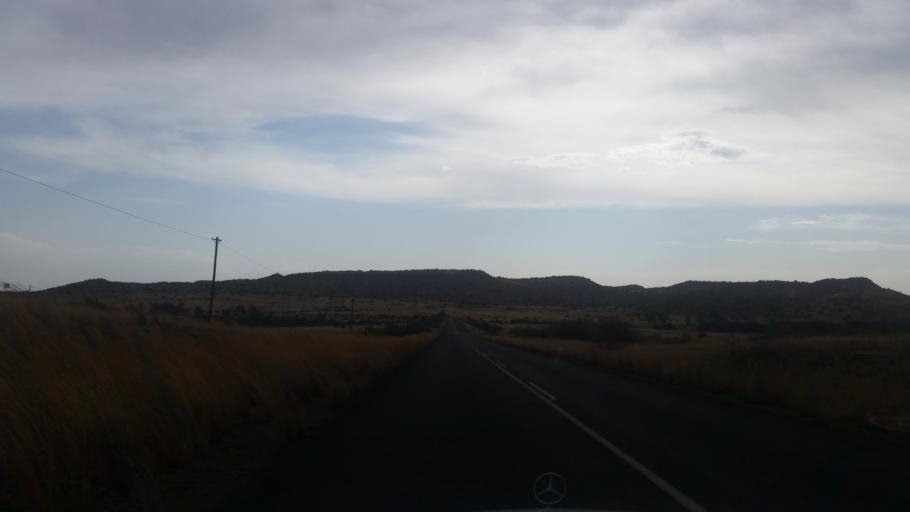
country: ZA
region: Orange Free State
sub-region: Xhariep District Municipality
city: Trompsburg
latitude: -30.4256
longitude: 26.1180
